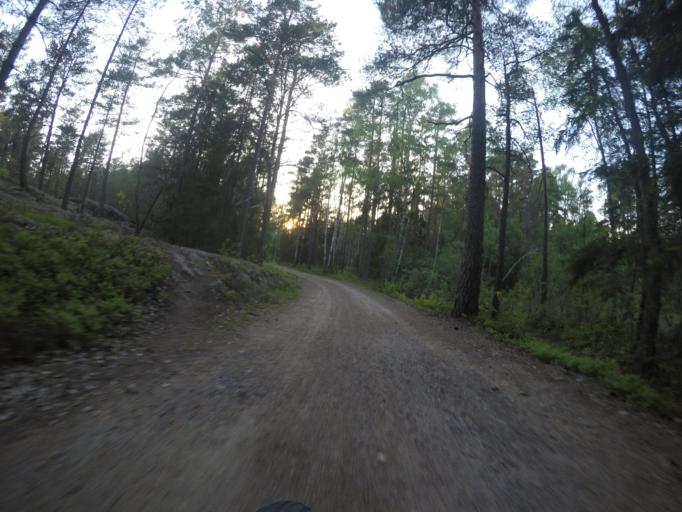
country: SE
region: Soedermanland
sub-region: Eskilstuna Kommun
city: Eskilstuna
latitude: 59.3431
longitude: 16.5120
